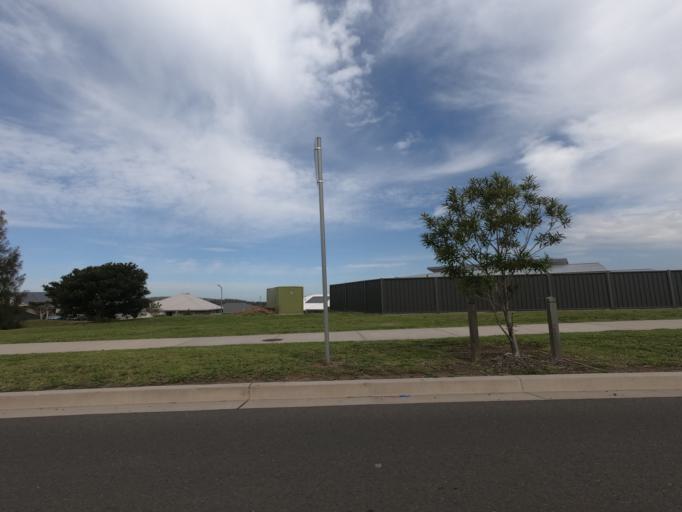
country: AU
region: New South Wales
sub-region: Wollongong
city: Dapto
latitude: -34.4942
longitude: 150.7602
